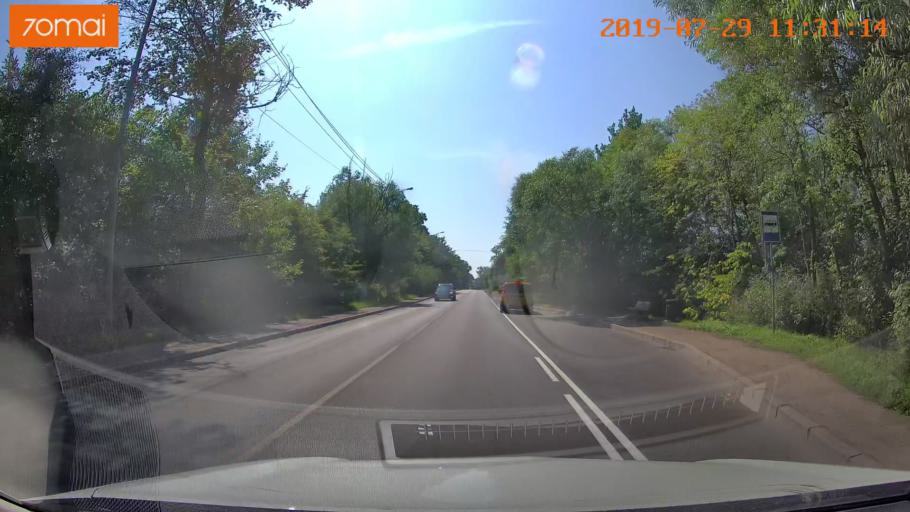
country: RU
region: Kaliningrad
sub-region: Gorod Kaliningrad
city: Kaliningrad
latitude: 54.6763
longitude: 20.5404
